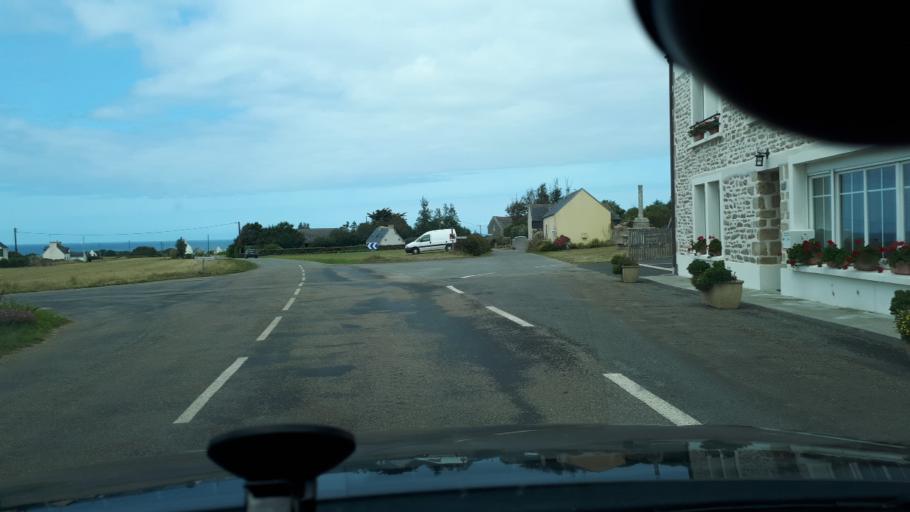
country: FR
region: Brittany
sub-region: Departement du Finistere
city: Plozevet
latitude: 47.9588
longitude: -4.3978
